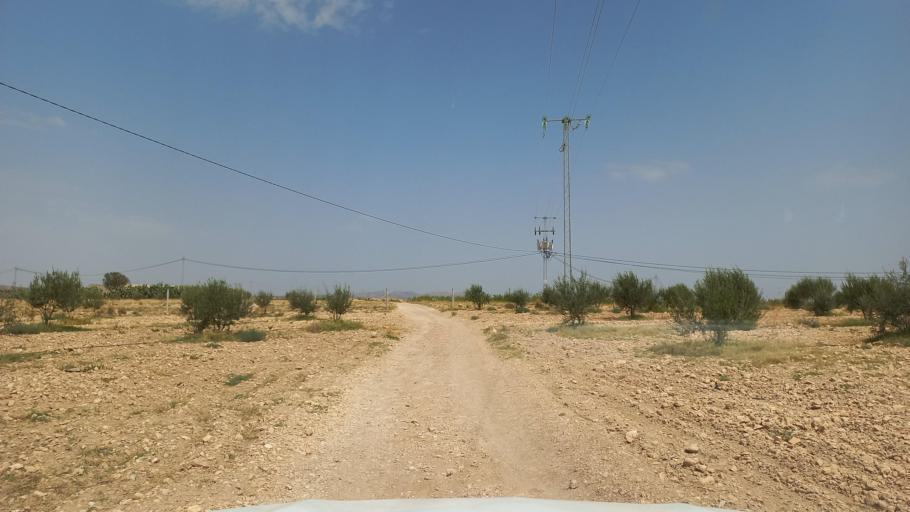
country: TN
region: Al Qasrayn
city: Kasserine
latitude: 35.2856
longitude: 9.0088
